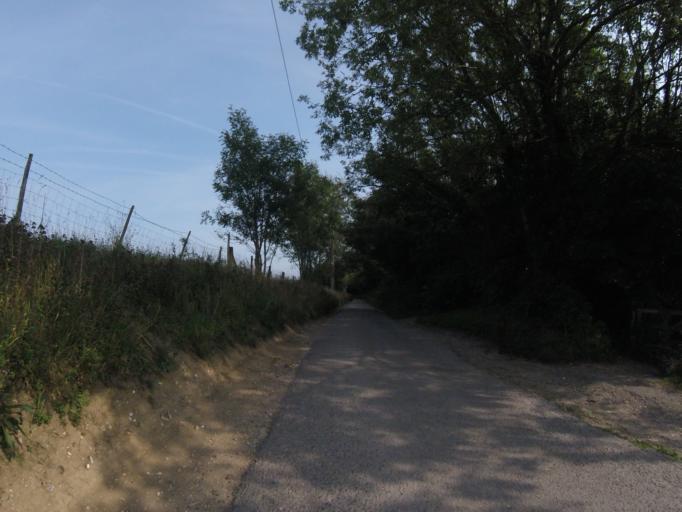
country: GB
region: England
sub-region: Brighton and Hove
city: Brighton
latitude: 50.8738
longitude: -0.1130
